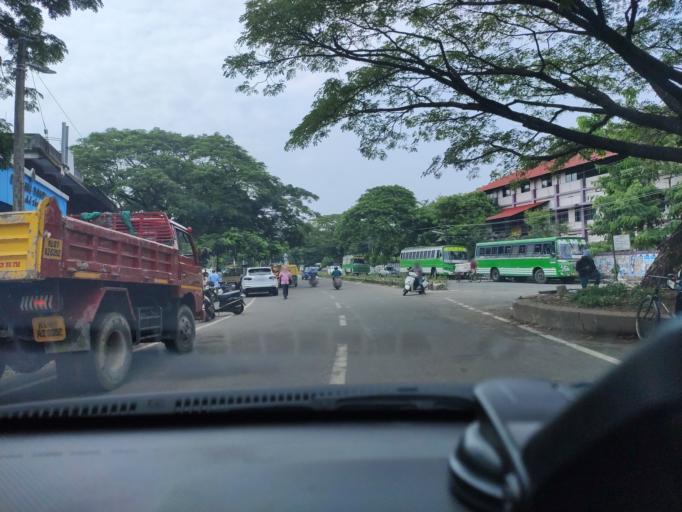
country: IN
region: Kerala
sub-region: Ernakulam
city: Elur
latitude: 10.0219
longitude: 76.3337
